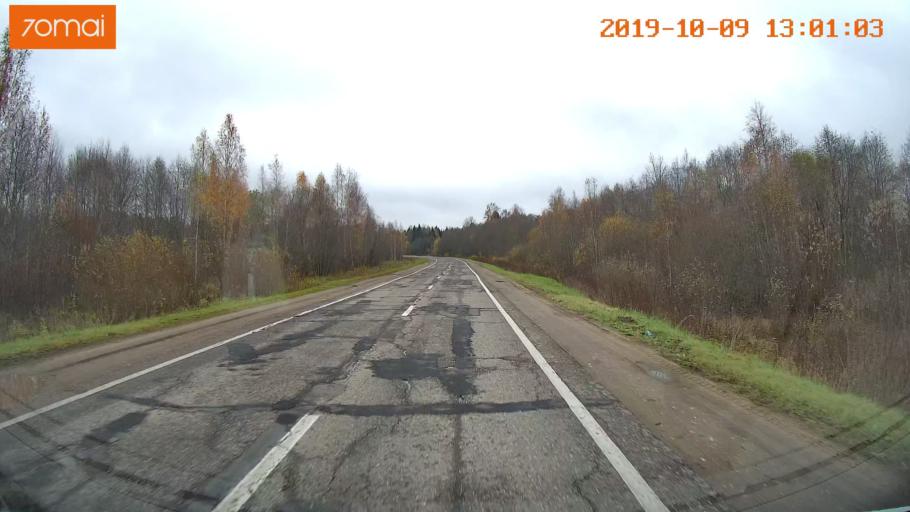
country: RU
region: Jaroslavl
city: Prechistoye
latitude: 58.3716
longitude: 40.4840
